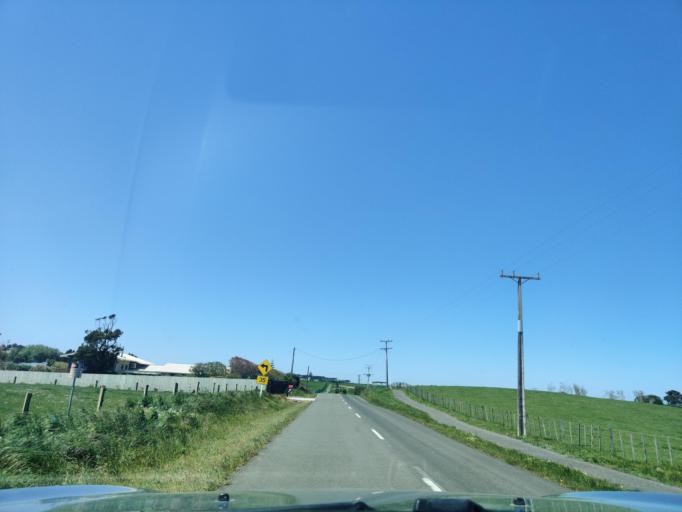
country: NZ
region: Taranaki
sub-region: South Taranaki District
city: Hawera
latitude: -39.6018
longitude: 174.2578
